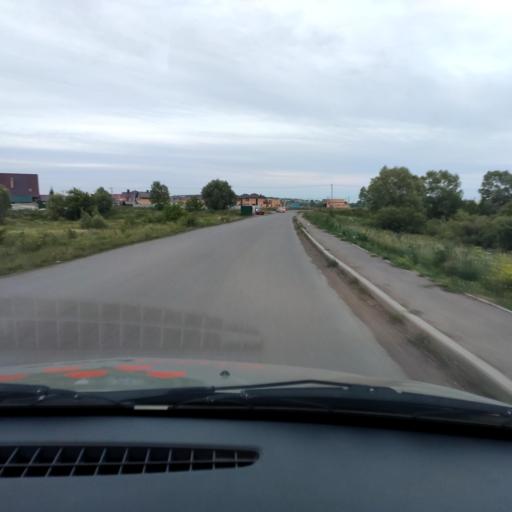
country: RU
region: Bashkortostan
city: Ufa
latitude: 54.6102
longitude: 55.9033
